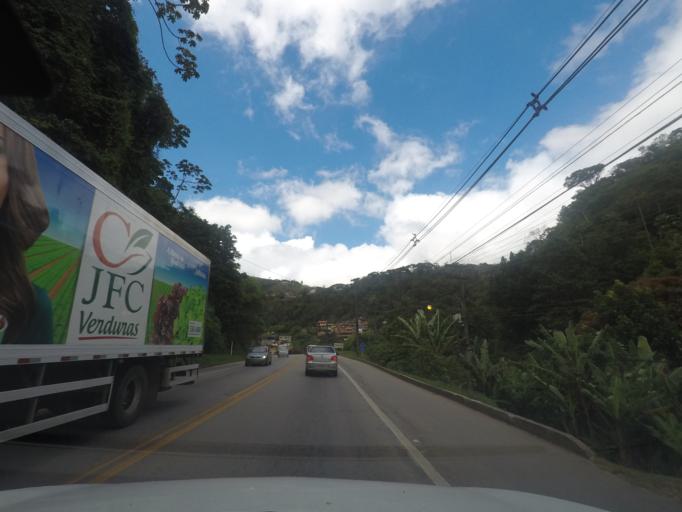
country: BR
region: Rio de Janeiro
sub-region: Teresopolis
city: Teresopolis
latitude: -22.3961
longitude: -42.9539
